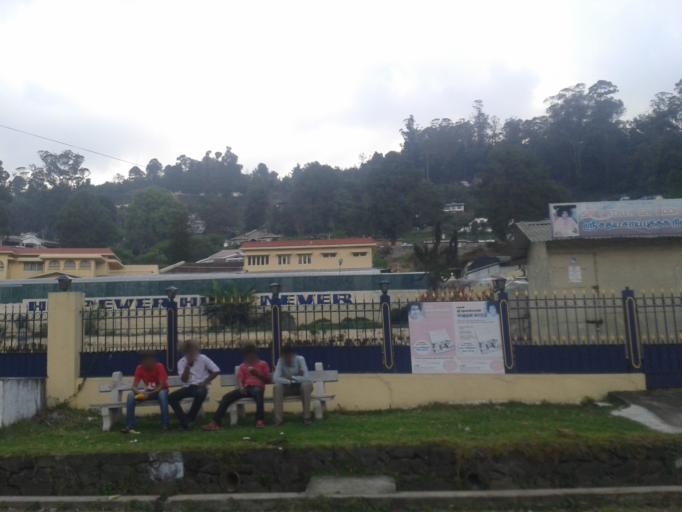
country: IN
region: Tamil Nadu
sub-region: Dindigul
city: Kodaikanal
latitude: 10.2338
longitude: 77.4821
